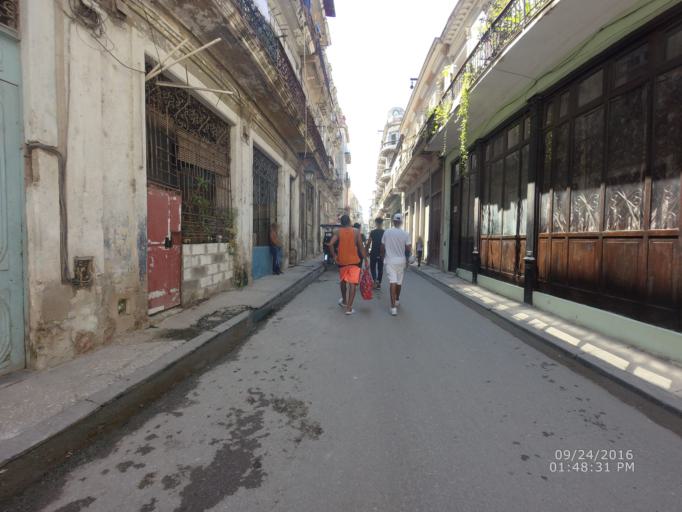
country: CU
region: La Habana
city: La Habana Vieja
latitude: 23.1348
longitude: -82.3526
